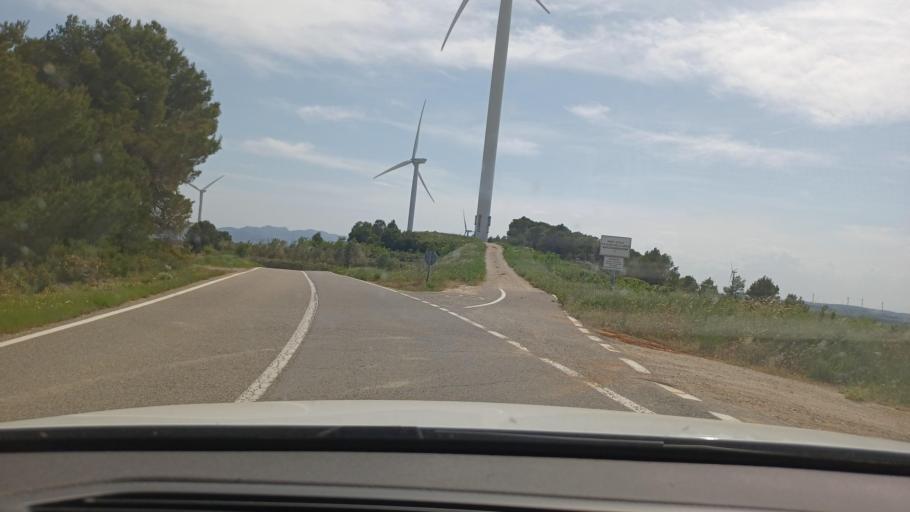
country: ES
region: Catalonia
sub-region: Provincia de Tarragona
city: Vilalba dels Arcs
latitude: 41.1055
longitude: 0.4179
